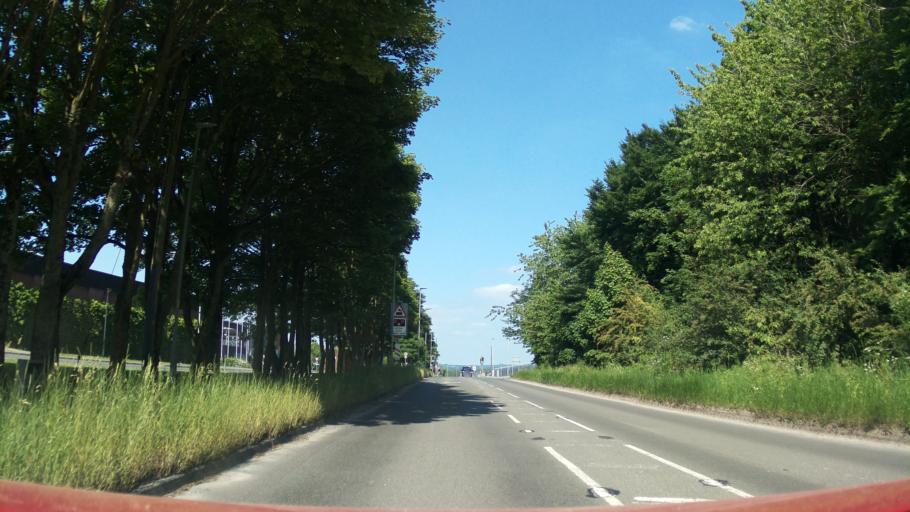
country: GB
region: England
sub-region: Wiltshire
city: Tidworth
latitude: 51.2505
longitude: -1.6382
